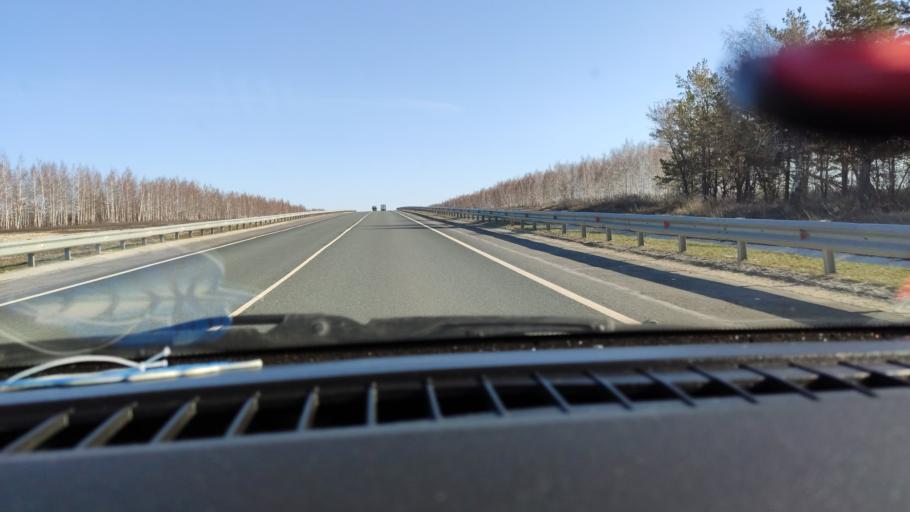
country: RU
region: Samara
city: Syzran'
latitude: 52.9030
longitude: 48.2972
